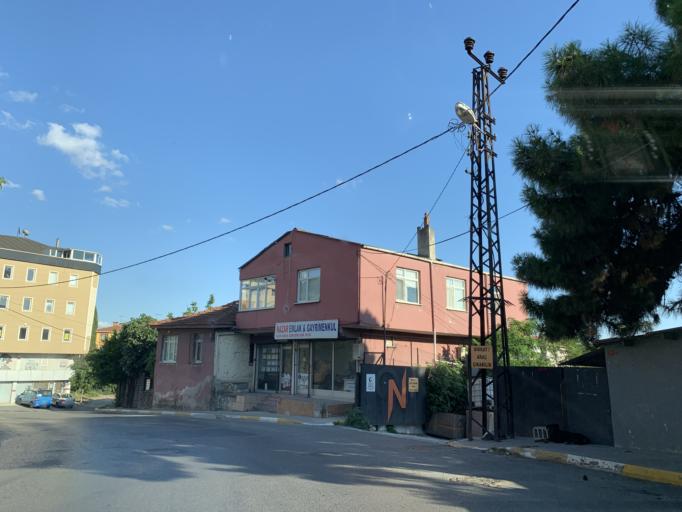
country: TR
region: Istanbul
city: Pendik
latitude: 40.9014
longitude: 29.2583
